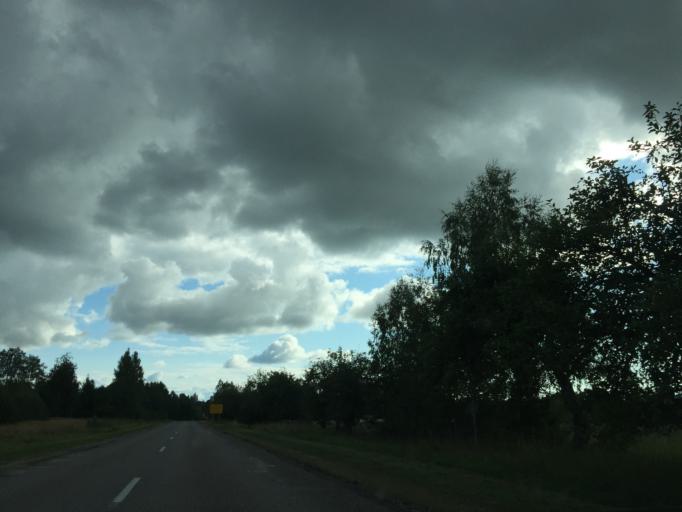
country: LV
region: Limbazu Rajons
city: Limbazi
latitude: 57.3583
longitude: 24.6691
